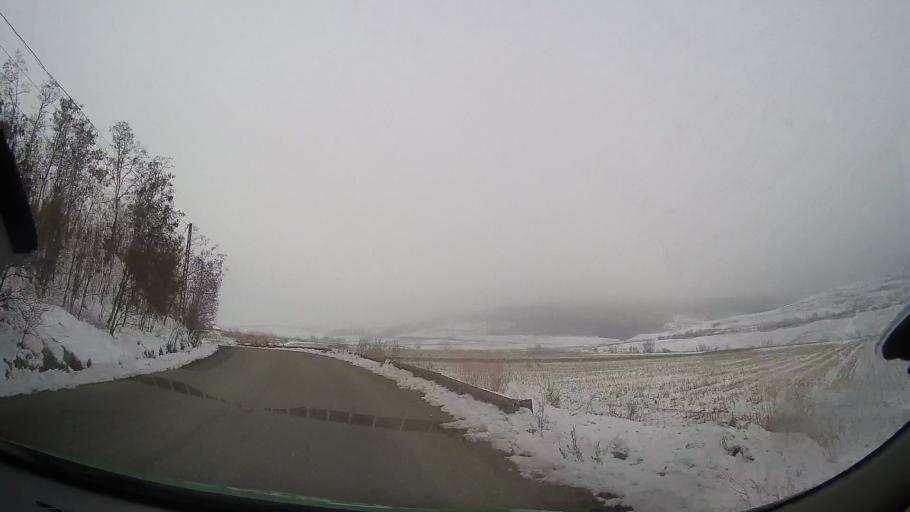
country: RO
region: Bacau
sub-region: Comuna Vultureni
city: Vultureni
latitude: 46.3531
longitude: 27.2886
